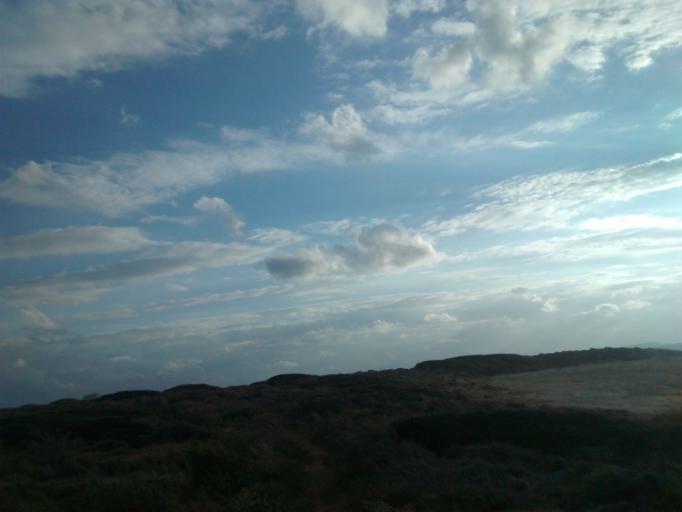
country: IT
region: Sardinia
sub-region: Provincia di Oristano
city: Narbolia
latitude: 40.0968
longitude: 8.4883
